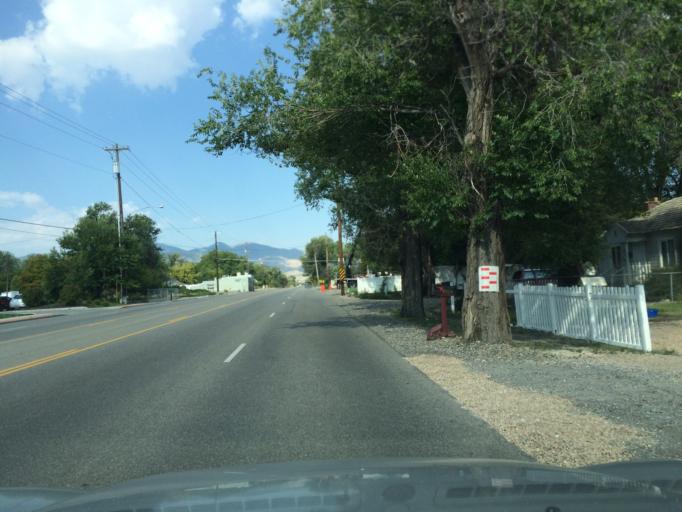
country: US
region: Utah
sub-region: Salt Lake County
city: West Valley City
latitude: 40.6966
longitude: -112.0156
